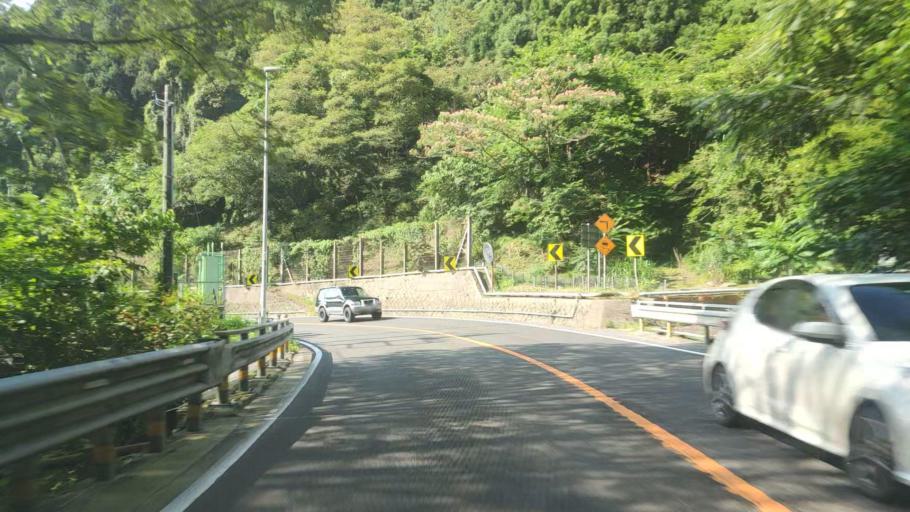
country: JP
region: Fukui
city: Tsuruga
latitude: 35.7707
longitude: 136.1069
